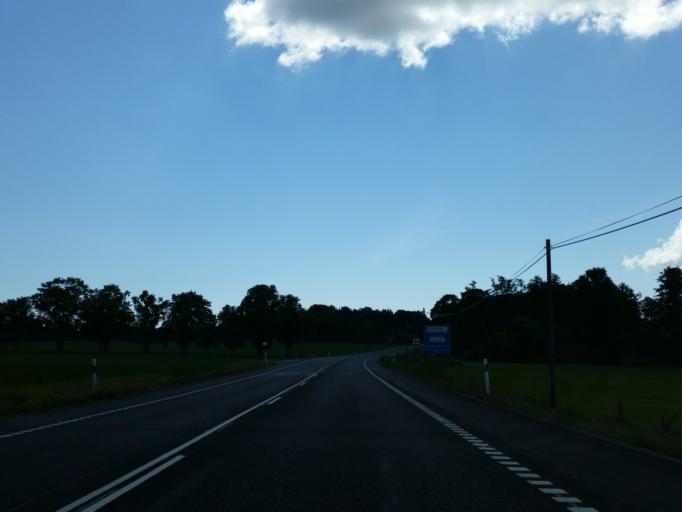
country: SE
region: Soedermanland
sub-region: Trosa Kommun
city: Vagnharad
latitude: 59.0100
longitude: 17.5961
